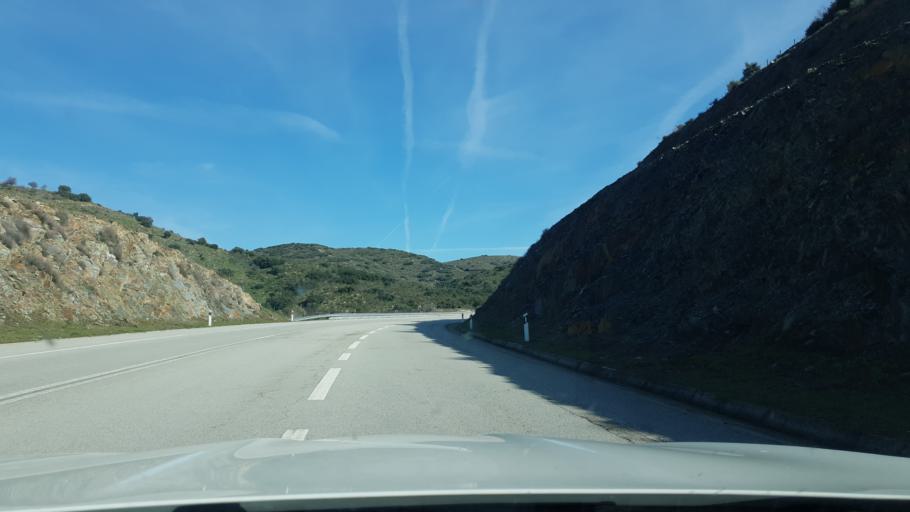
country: PT
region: Braganca
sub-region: Torre de Moncorvo
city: Torre de Moncorvo
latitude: 41.1833
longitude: -7.0963
